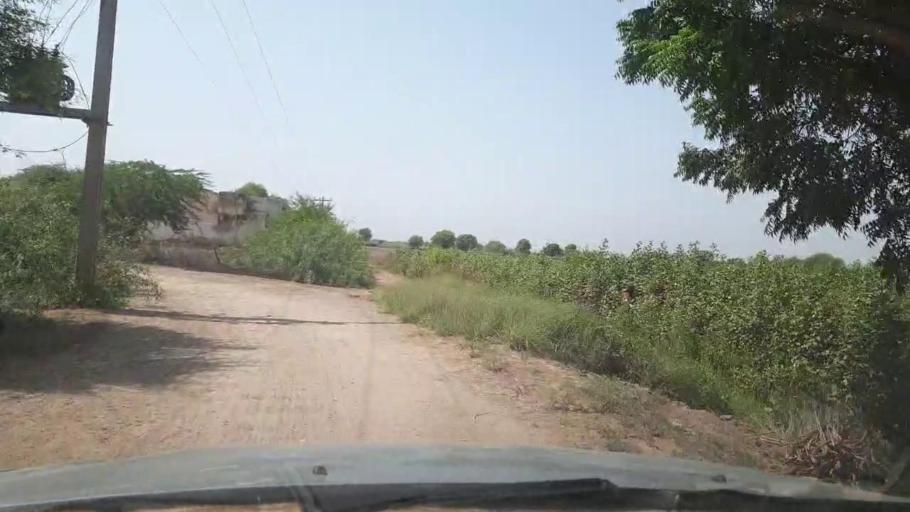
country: PK
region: Sindh
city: Chambar
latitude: 25.2071
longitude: 68.7818
